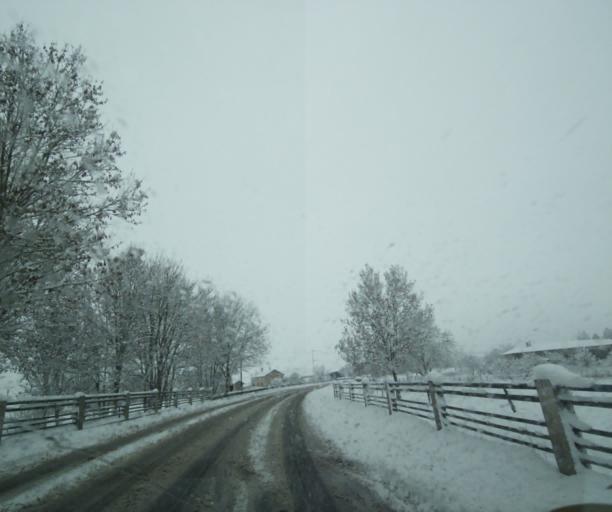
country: FR
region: Champagne-Ardenne
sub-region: Departement de la Haute-Marne
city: Saint-Dizier
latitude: 48.5849
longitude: 4.9015
